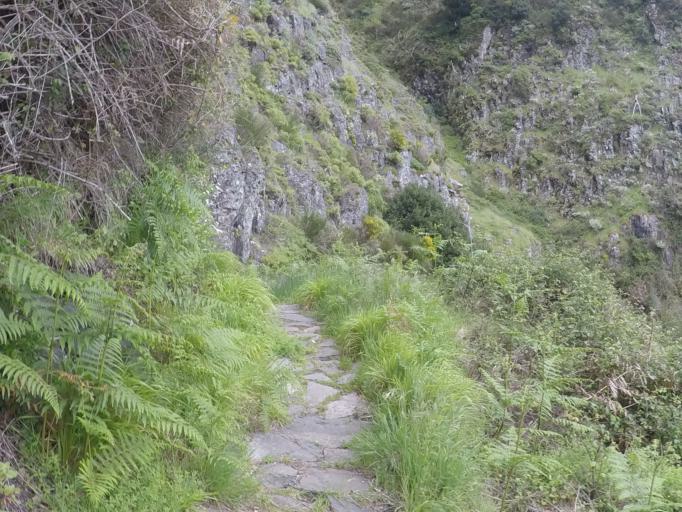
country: PT
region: Madeira
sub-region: Camara de Lobos
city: Curral das Freiras
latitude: 32.7370
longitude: -17.0001
